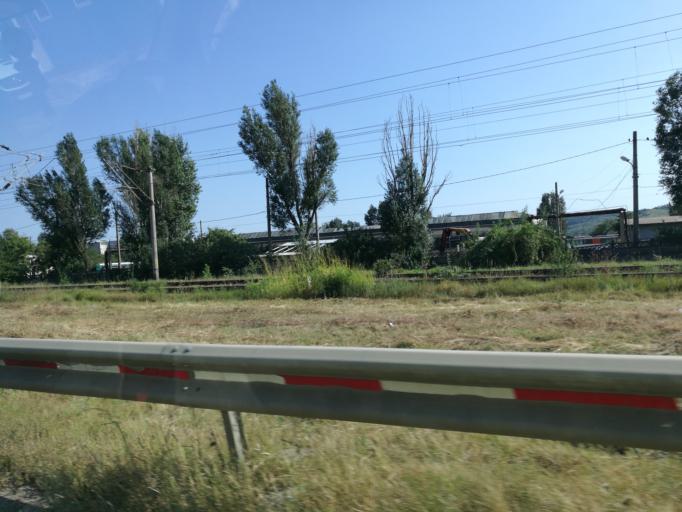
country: RO
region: Iasi
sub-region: Comuna Miroslava
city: Miroslava
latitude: 47.1722
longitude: 27.5335
